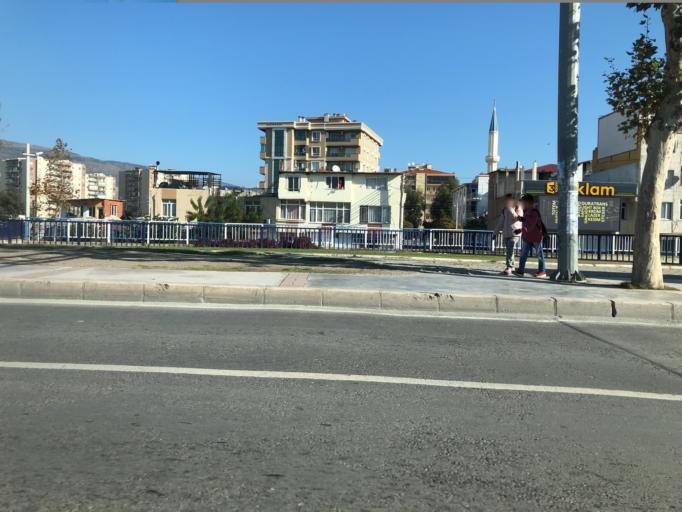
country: TR
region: Izmir
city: Izmir
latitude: 38.4611
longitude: 27.1726
